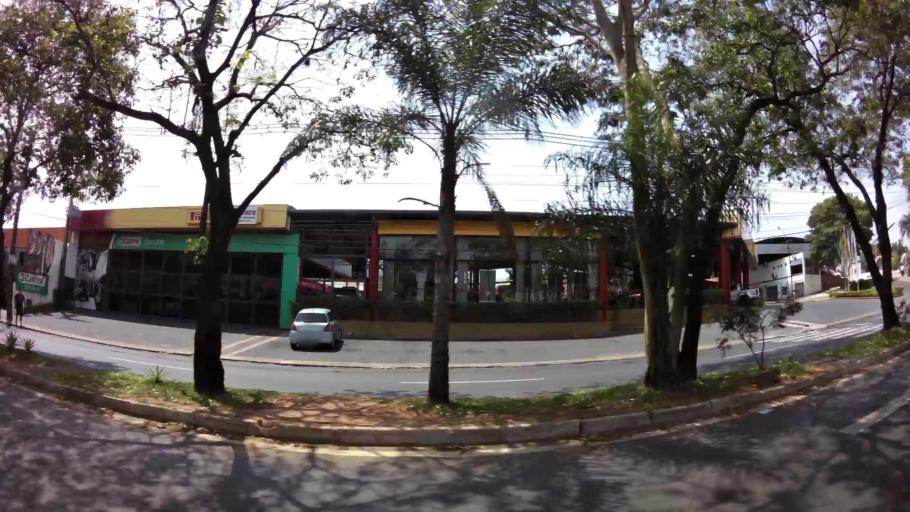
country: PY
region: Asuncion
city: Asuncion
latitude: -25.2892
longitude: -57.5896
